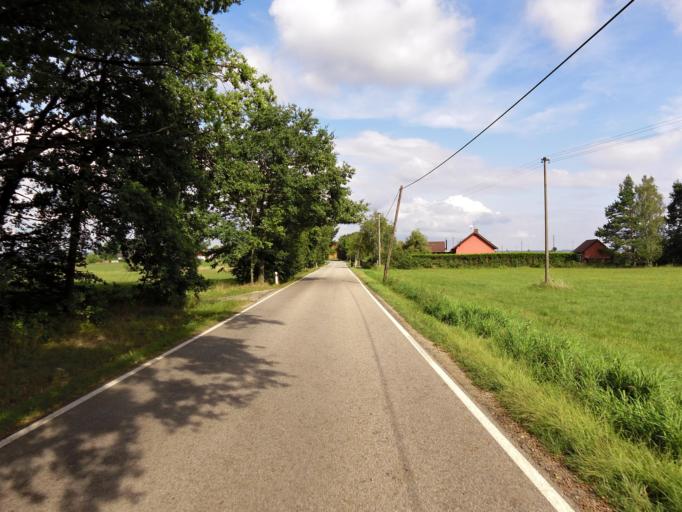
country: CZ
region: Jihocesky
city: Suchdol nad Luznici
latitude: 48.8887
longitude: 14.8399
